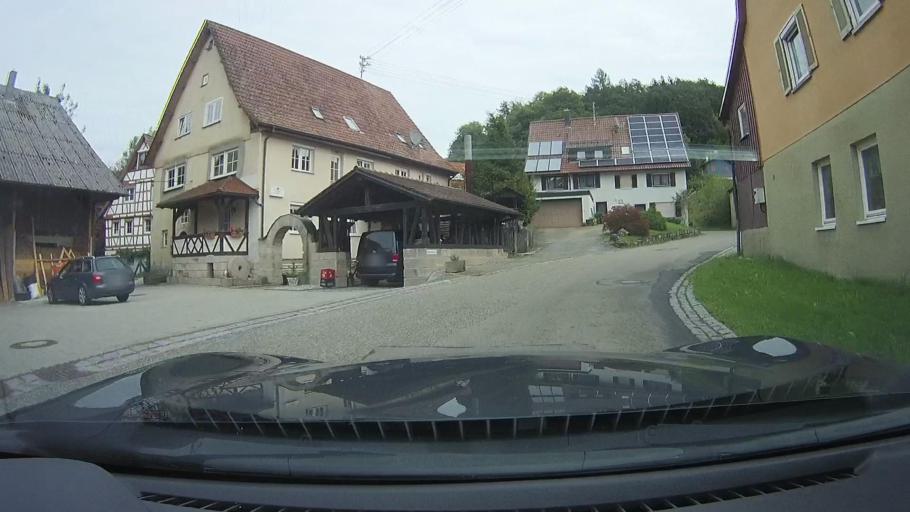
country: DE
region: Baden-Wuerttemberg
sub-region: Regierungsbezirk Stuttgart
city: Sulzbach an der Murr
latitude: 48.9972
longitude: 9.5340
